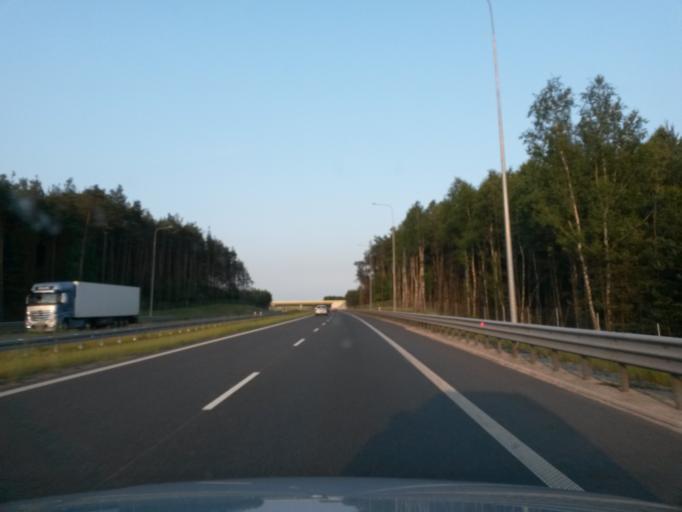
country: PL
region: Lodz Voivodeship
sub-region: Powiat wieruszowski
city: Wieruszow
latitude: 51.3060
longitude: 18.1942
